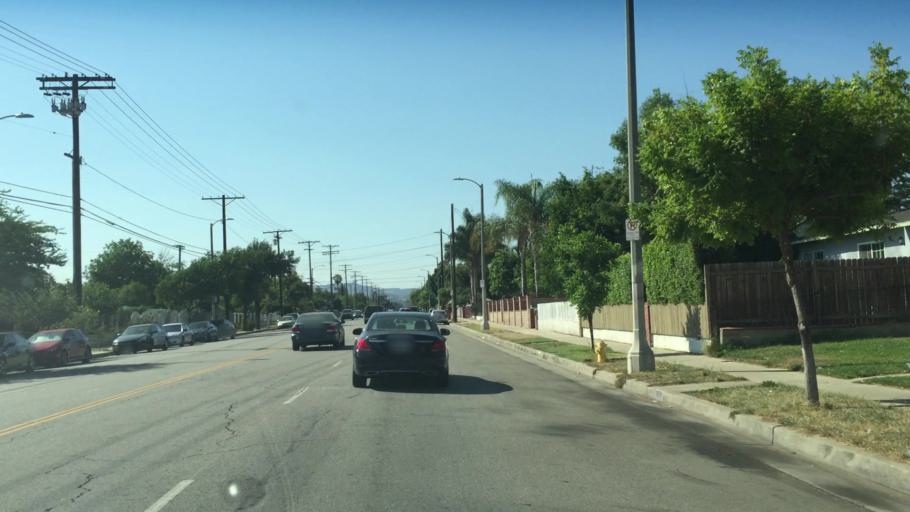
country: US
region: California
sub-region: Los Angeles County
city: San Fernando
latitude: 34.2440
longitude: -118.4280
